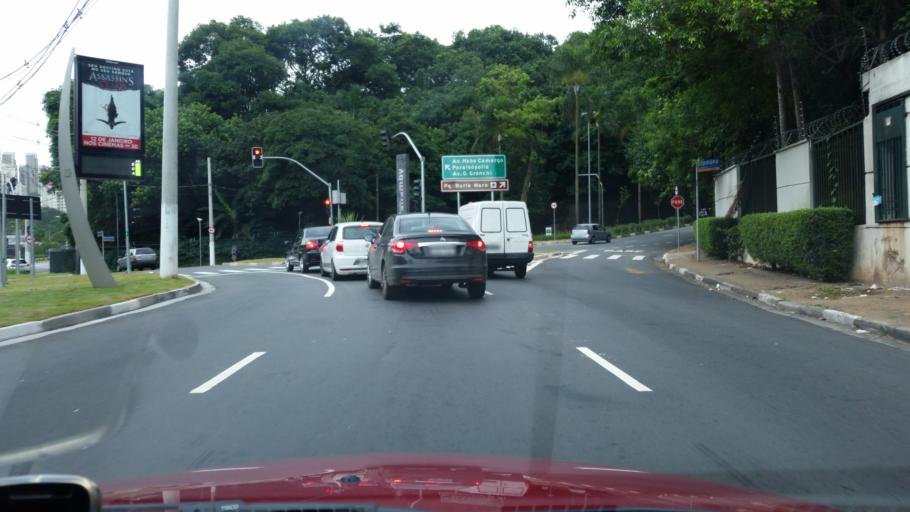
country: BR
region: Sao Paulo
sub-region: Taboao Da Serra
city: Taboao da Serra
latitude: -23.6353
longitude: -46.7270
